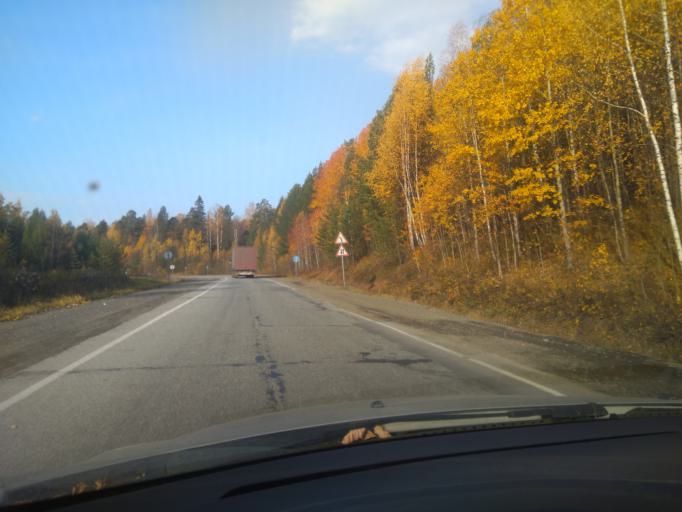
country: RU
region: Sverdlovsk
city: Druzhinino
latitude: 56.8004
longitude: 59.4670
